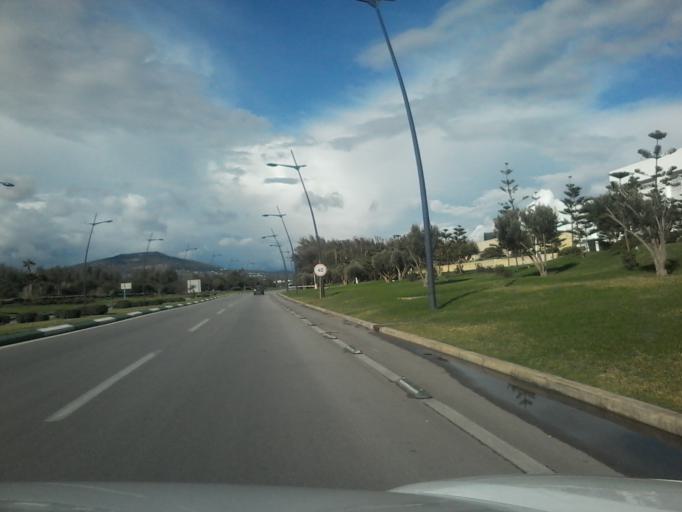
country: MA
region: Tanger-Tetouan
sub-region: Tetouan
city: Martil
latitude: 35.6949
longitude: -5.3295
